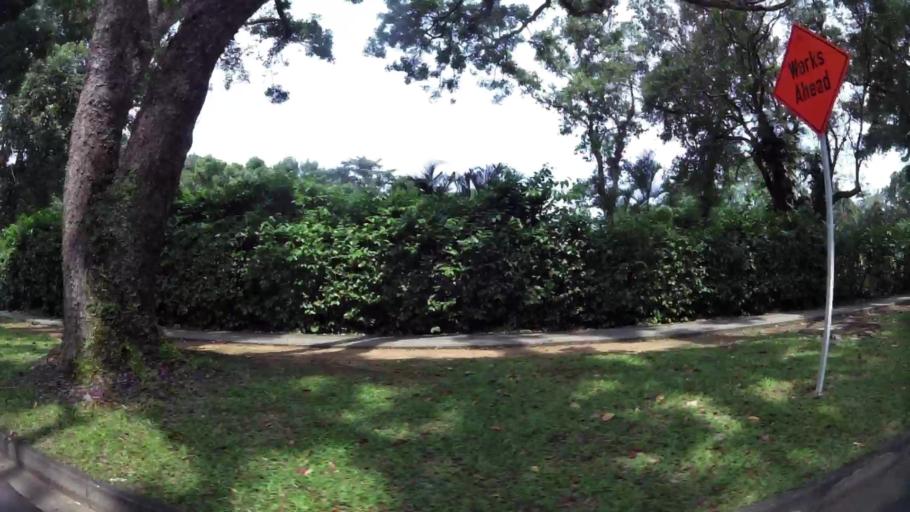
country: MY
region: Johor
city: Kampung Pasir Gudang Baru
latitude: 1.3879
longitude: 103.9847
